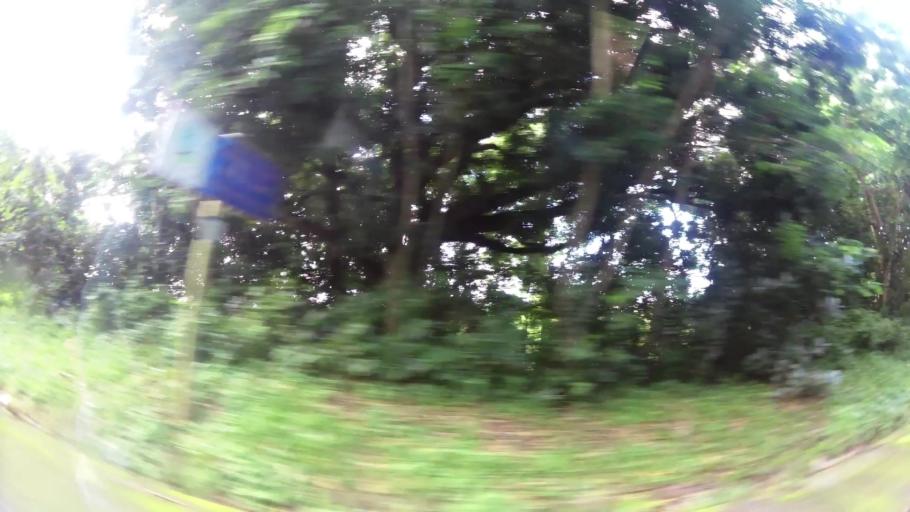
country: MQ
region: Martinique
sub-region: Martinique
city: Le Francois
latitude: 14.6026
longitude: -60.9379
